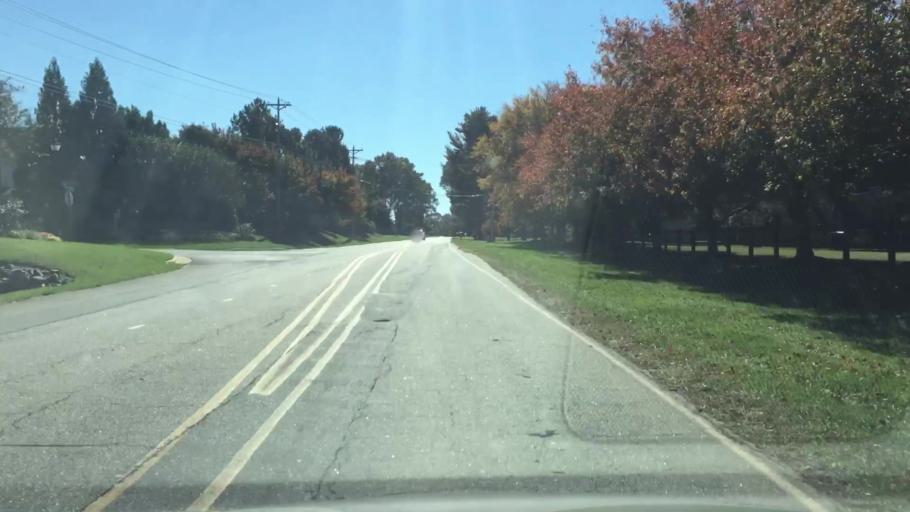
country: US
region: North Carolina
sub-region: Iredell County
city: Mooresville
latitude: 35.5456
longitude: -80.7895
